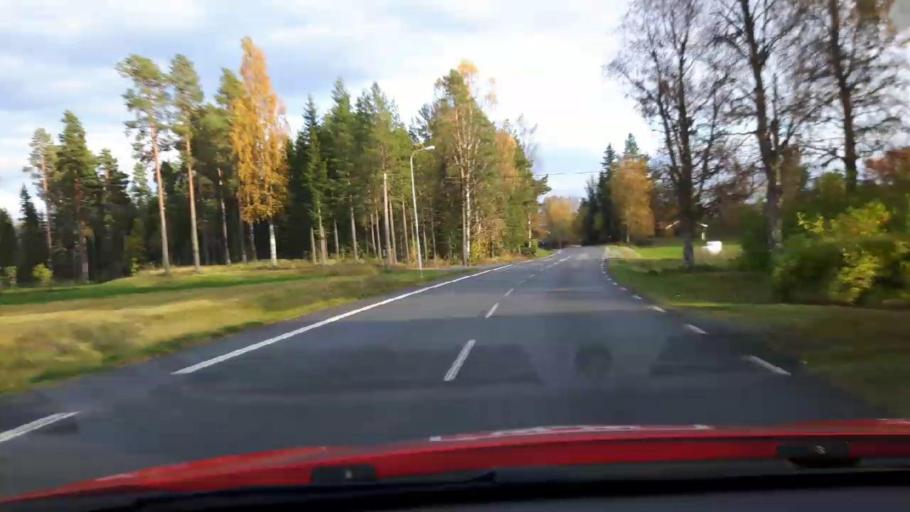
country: SE
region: Jaemtland
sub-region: Krokoms Kommun
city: Krokom
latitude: 63.3466
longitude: 14.5627
